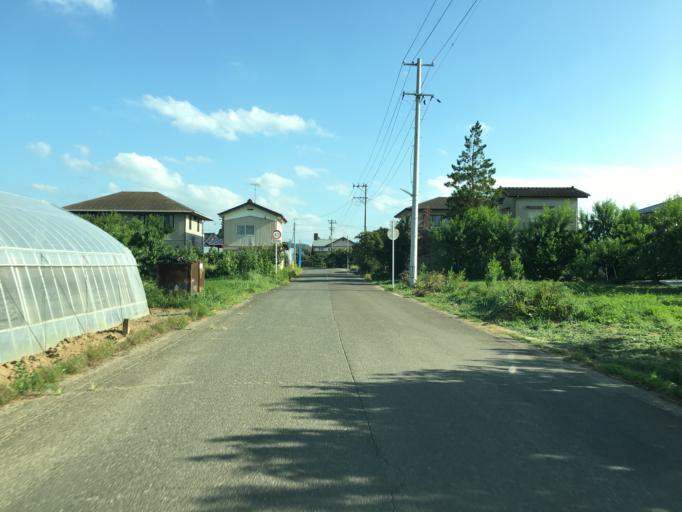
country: JP
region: Fukushima
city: Yanagawamachi-saiwaicho
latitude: 37.8382
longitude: 140.5838
